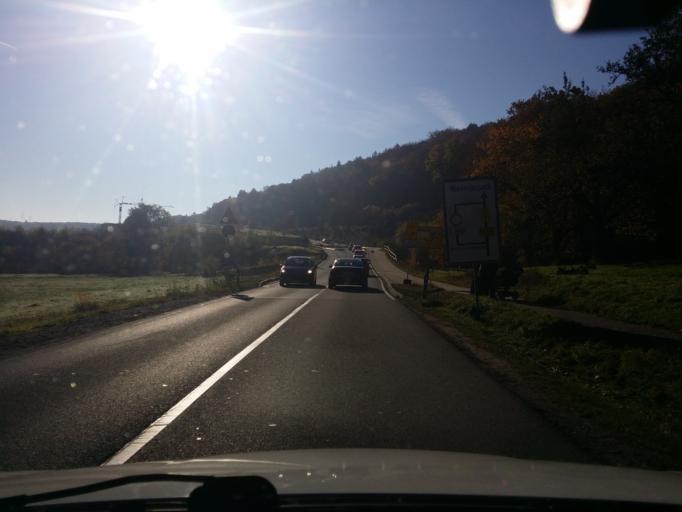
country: DE
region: Hesse
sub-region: Regierungsbezirk Darmstadt
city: Niedernhausen
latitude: 50.1551
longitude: 8.3227
